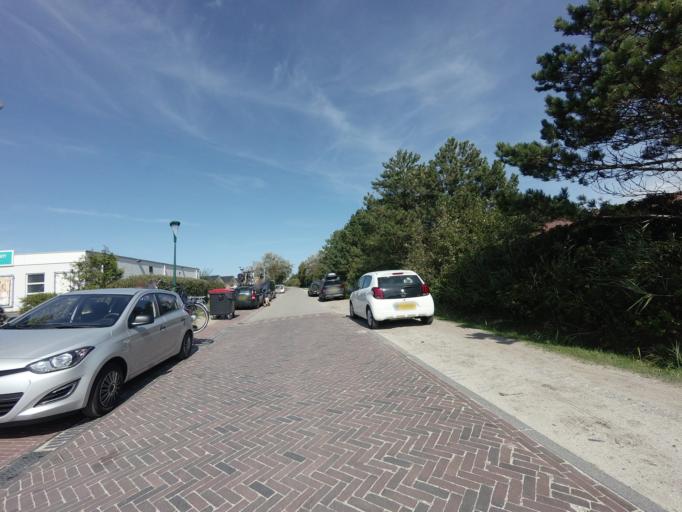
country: NL
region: Friesland
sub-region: Gemeente Ameland
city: Hollum
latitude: 53.4503
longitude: 5.6377
